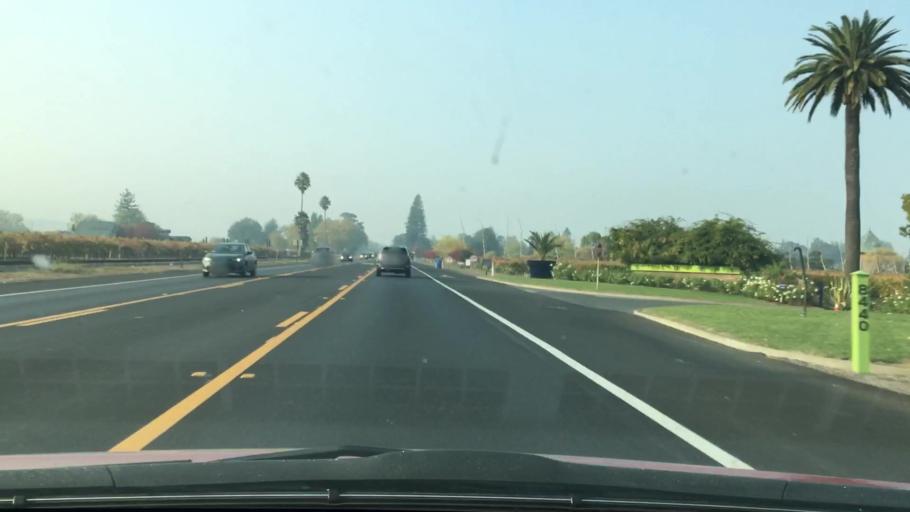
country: US
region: California
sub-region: Napa County
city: Saint Helena
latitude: 38.4531
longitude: -122.4172
